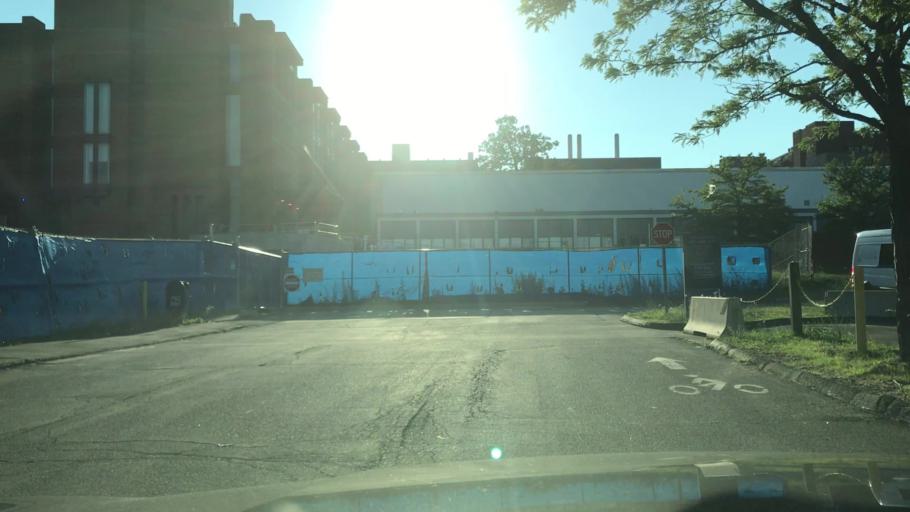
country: US
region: Connecticut
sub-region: New Haven County
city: New Haven
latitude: 41.3180
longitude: -72.9205
